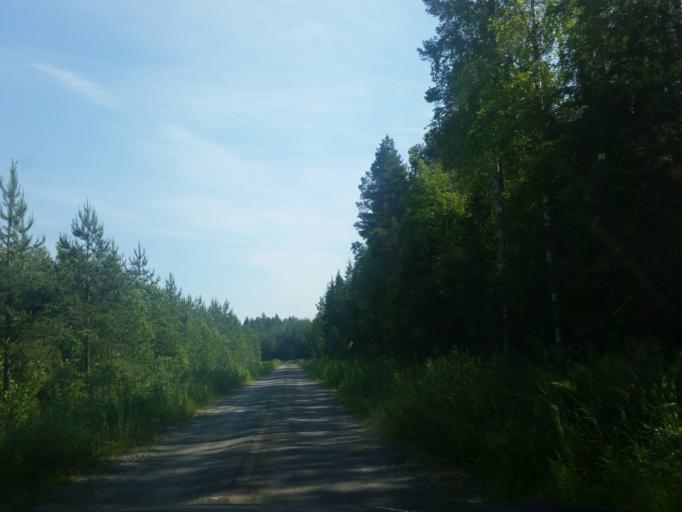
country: FI
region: Northern Savo
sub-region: Ylae-Savo
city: Keitele
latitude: 63.1022
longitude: 26.5450
